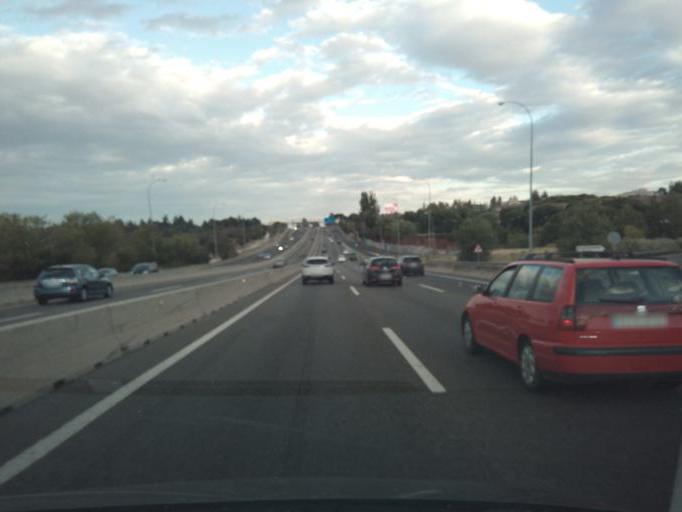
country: ES
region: Madrid
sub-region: Provincia de Madrid
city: Majadahonda
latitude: 40.4784
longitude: -3.8457
